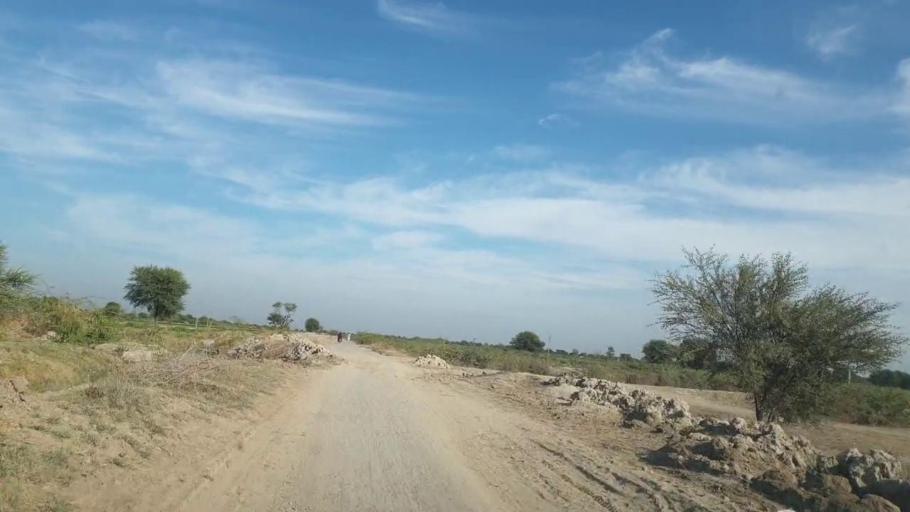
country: PK
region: Sindh
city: Pithoro
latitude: 25.6455
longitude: 69.3589
